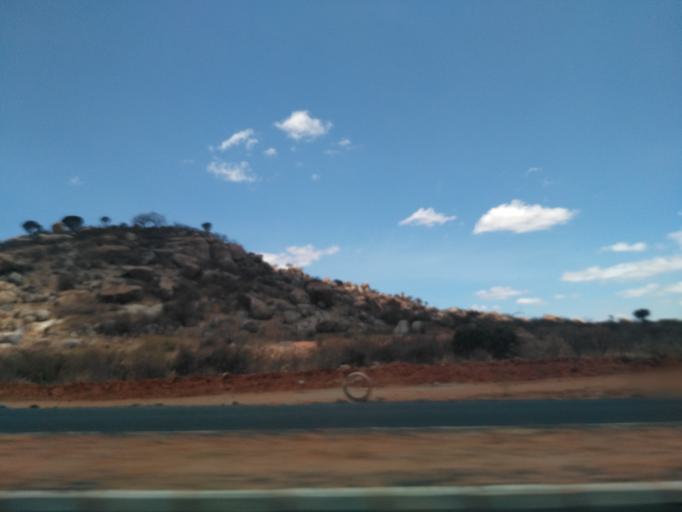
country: TZ
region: Dodoma
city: Kisasa
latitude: -6.1840
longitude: 35.8383
